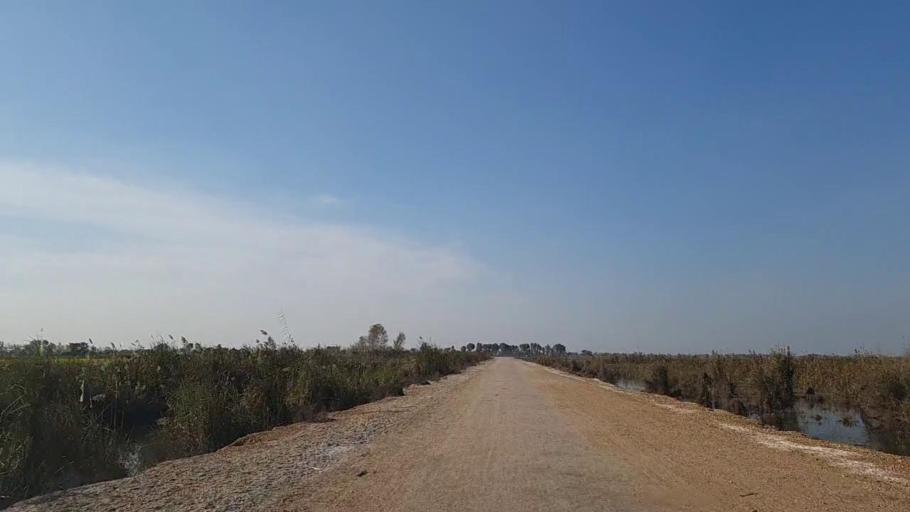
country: PK
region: Sindh
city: Bandhi
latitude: 26.6087
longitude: 68.3121
